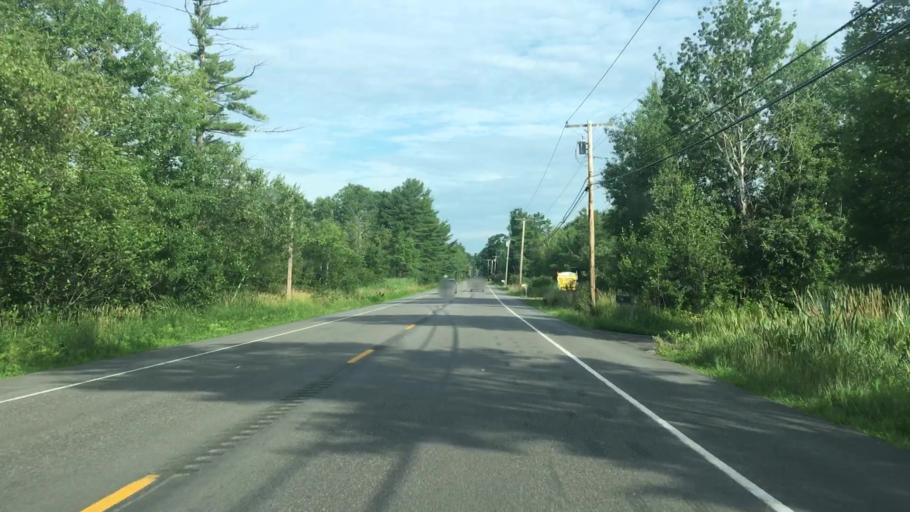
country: US
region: Maine
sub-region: York County
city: Buxton
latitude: 43.7088
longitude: -70.5103
